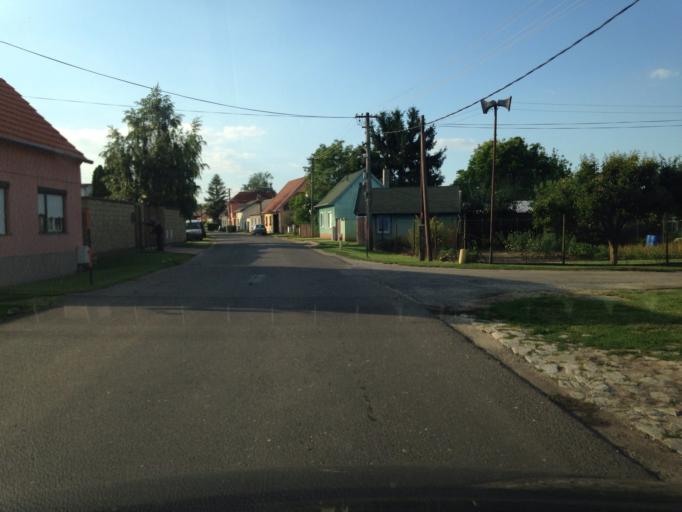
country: AT
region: Lower Austria
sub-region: Politischer Bezirk Ganserndorf
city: Angern an der March
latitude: 48.4037
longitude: 16.8603
